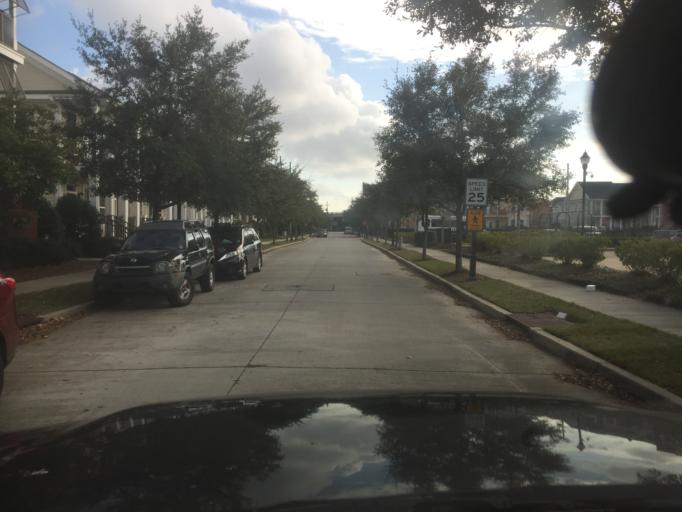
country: US
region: Louisiana
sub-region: Orleans Parish
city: New Orleans
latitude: 29.9957
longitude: -90.0771
